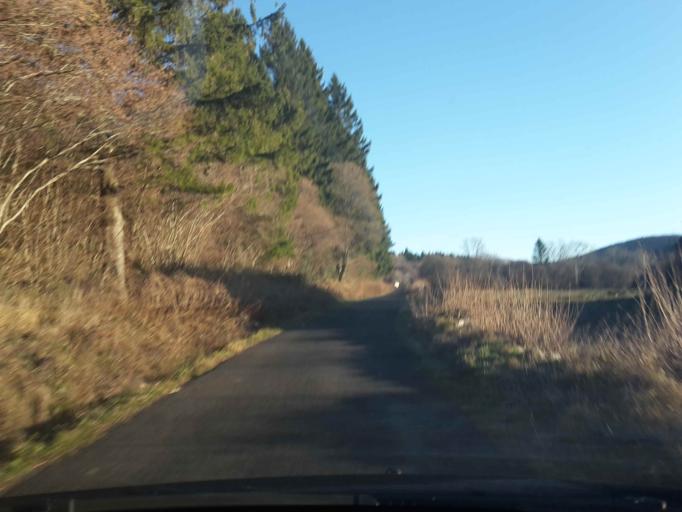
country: FR
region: Auvergne
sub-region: Departement du Cantal
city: Riom-es-Montagnes
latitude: 45.2321
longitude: 2.5597
